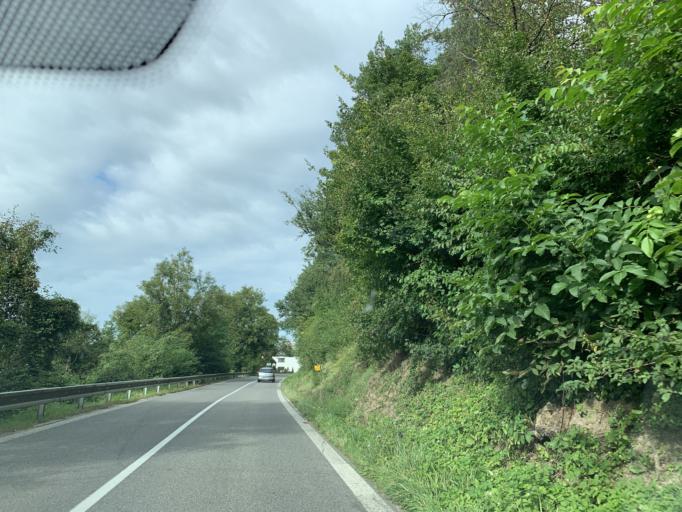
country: SK
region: Trenciansky
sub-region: Okres Nove Mesto nad Vahom
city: Nove Mesto nad Vahom
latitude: 48.8202
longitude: 17.9380
